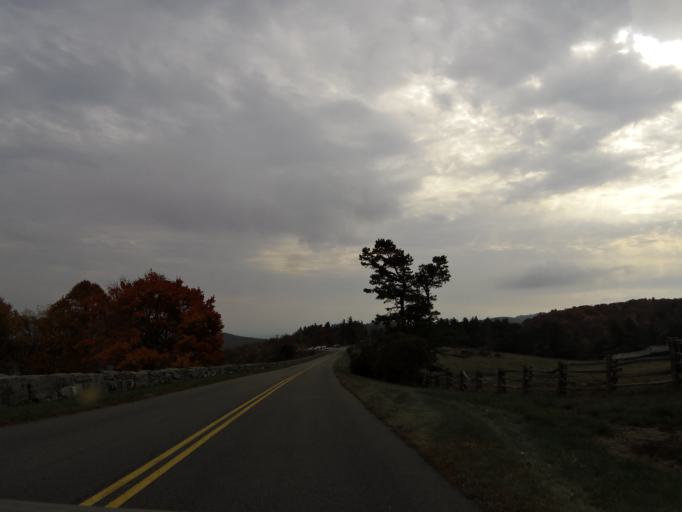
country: US
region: North Carolina
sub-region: Alleghany County
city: Sparta
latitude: 36.4111
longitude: -81.1951
